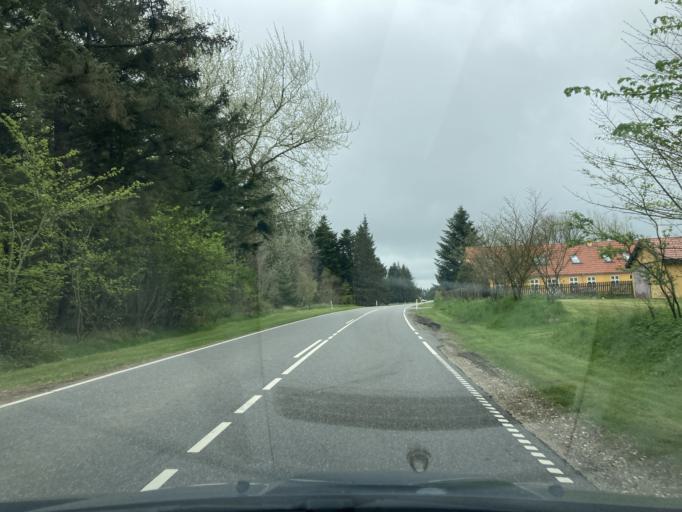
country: DK
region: North Denmark
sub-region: Thisted Kommune
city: Hurup
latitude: 56.8733
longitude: 8.3857
